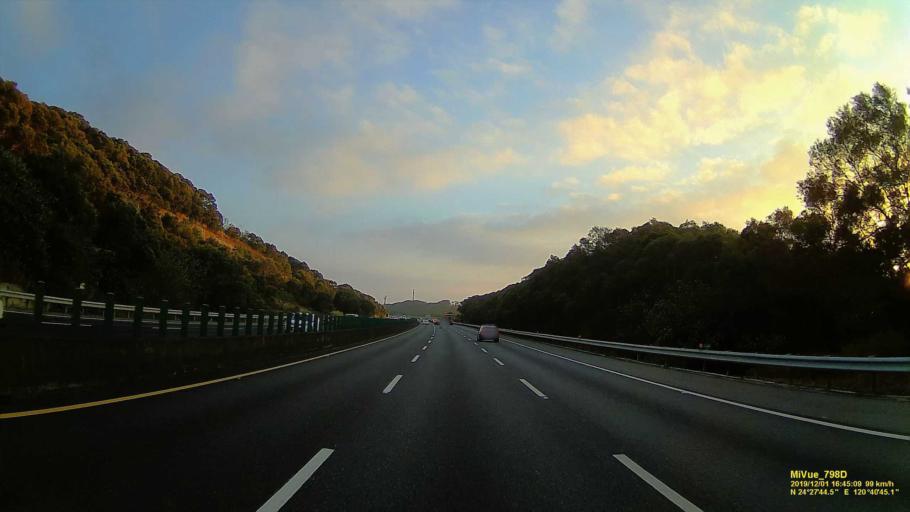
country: TW
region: Taiwan
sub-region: Miaoli
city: Miaoli
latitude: 24.4638
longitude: 120.6797
